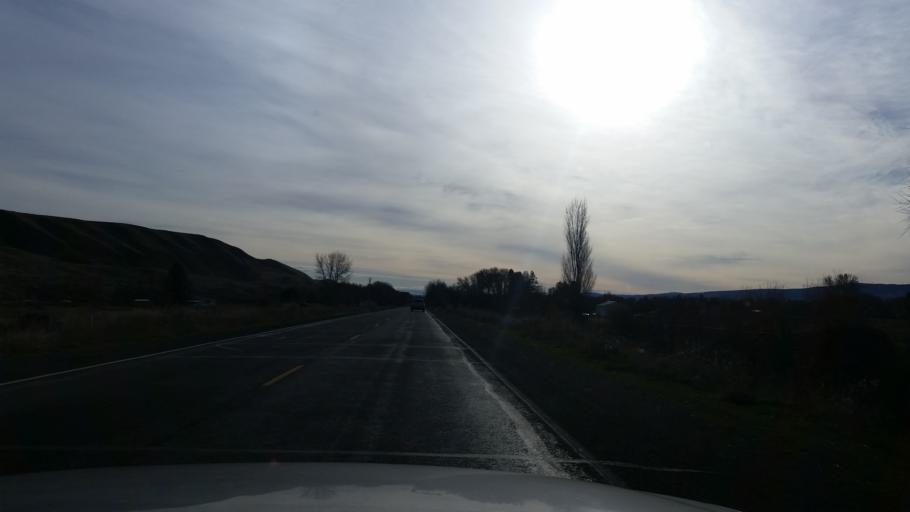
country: US
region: Washington
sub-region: Kittitas County
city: Ellensburg
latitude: 47.0931
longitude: -120.6854
